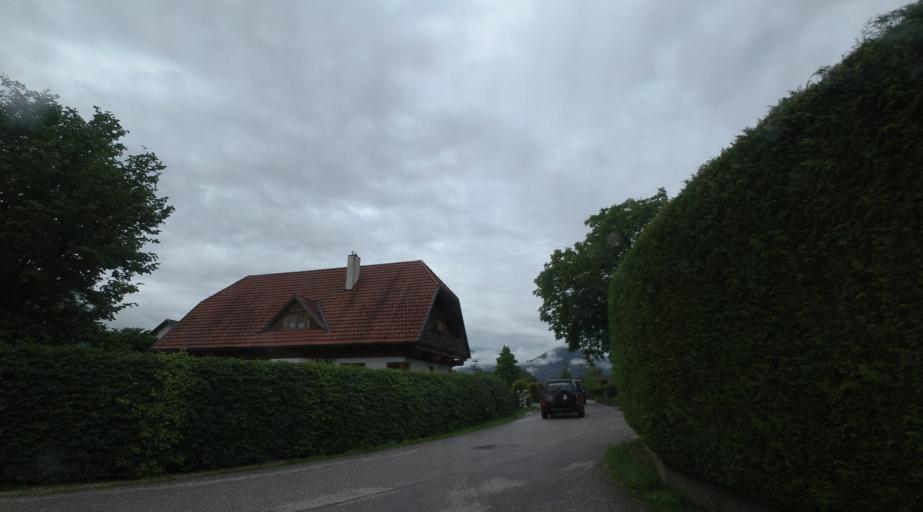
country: AT
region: Upper Austria
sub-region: Politischer Bezirk Kirchdorf an der Krems
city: Gruenburg
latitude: 47.8930
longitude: 14.2781
